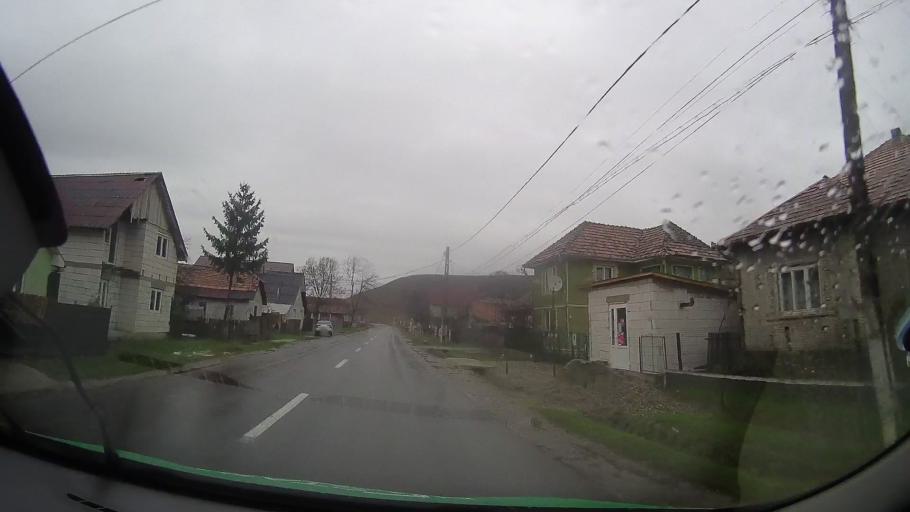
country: RO
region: Bistrita-Nasaud
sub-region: Comuna Mariselu
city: Mariselu
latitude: 47.0416
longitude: 24.4724
